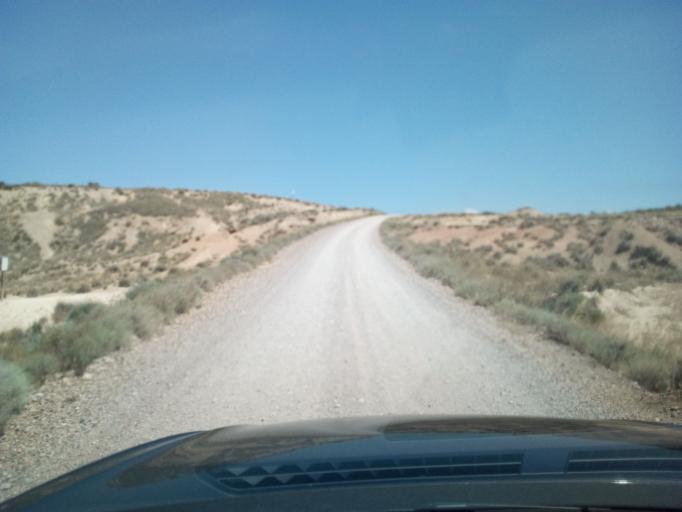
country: ES
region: Navarre
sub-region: Provincia de Navarra
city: Fustinana
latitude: 42.1666
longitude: -1.4268
